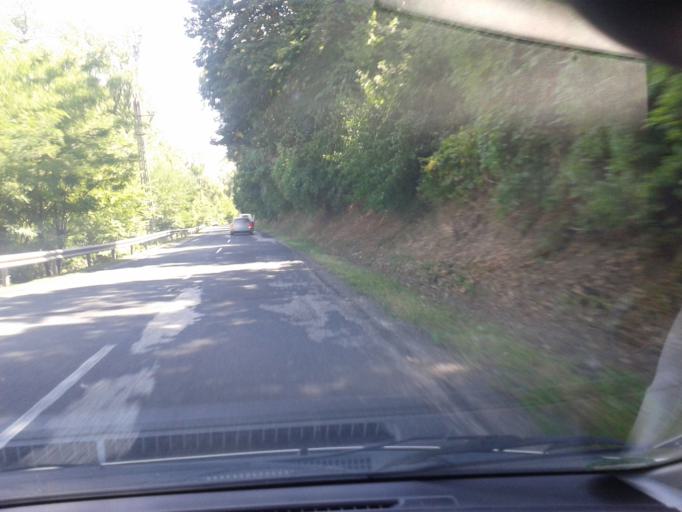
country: HU
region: Pest
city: Szob
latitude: 47.8137
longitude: 18.8270
